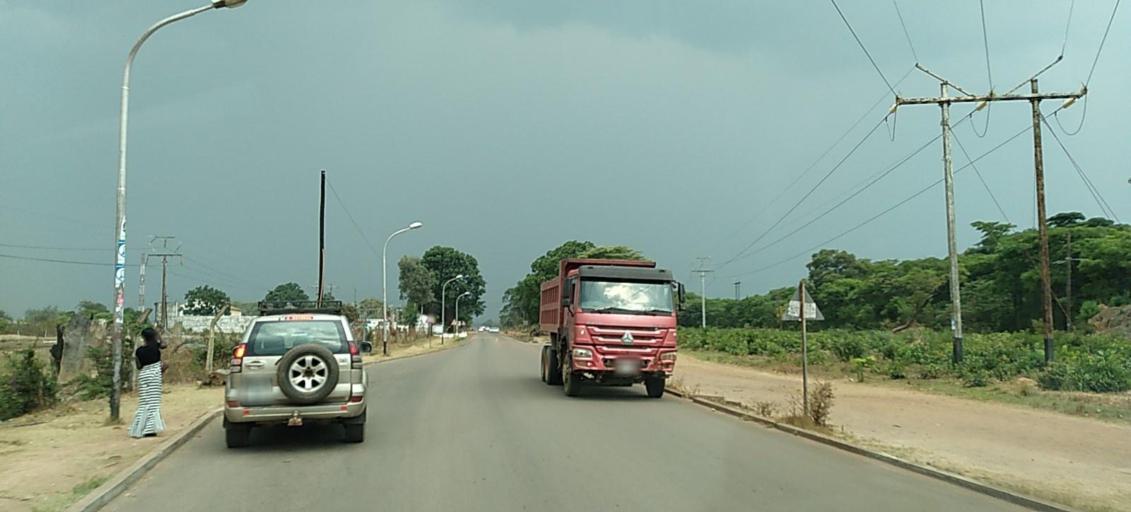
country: ZM
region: Copperbelt
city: Kalulushi
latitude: -12.8327
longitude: 28.1030
